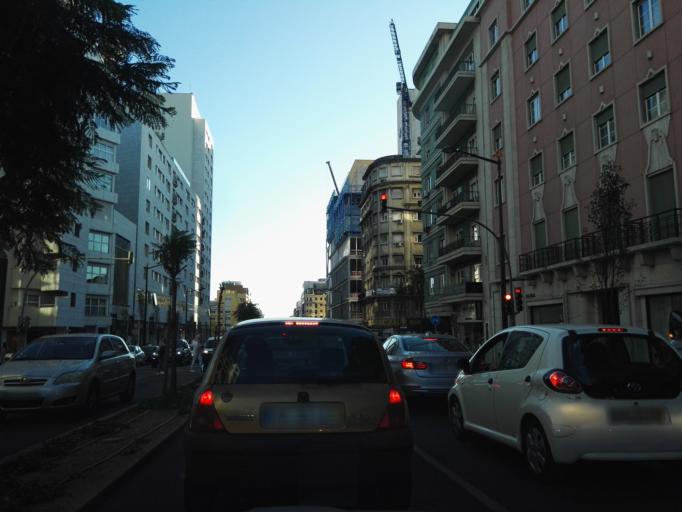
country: PT
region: Lisbon
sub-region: Lisbon
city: Lisbon
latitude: 38.7330
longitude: -9.1454
